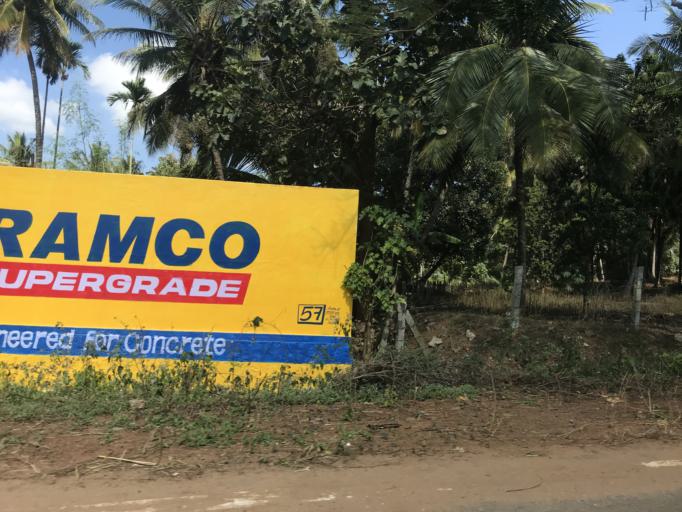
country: IN
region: Karnataka
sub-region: Mysore
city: Heggadadevankote
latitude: 12.1159
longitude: 76.3131
